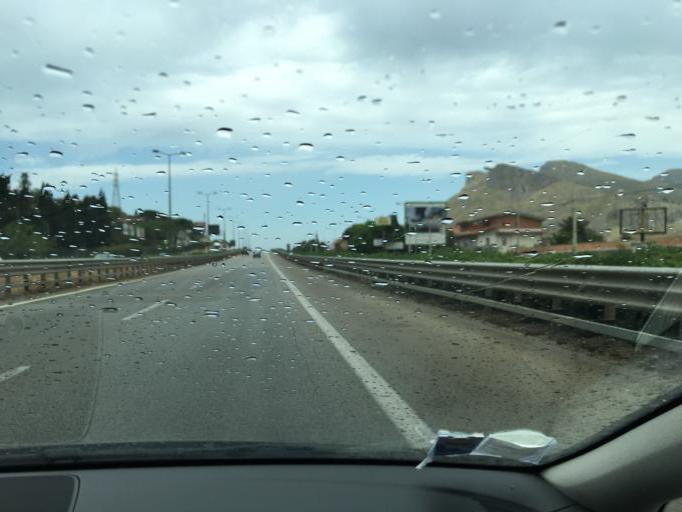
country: IT
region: Sicily
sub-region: Palermo
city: Isola delle Femmine
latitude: 38.1808
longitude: 13.2923
